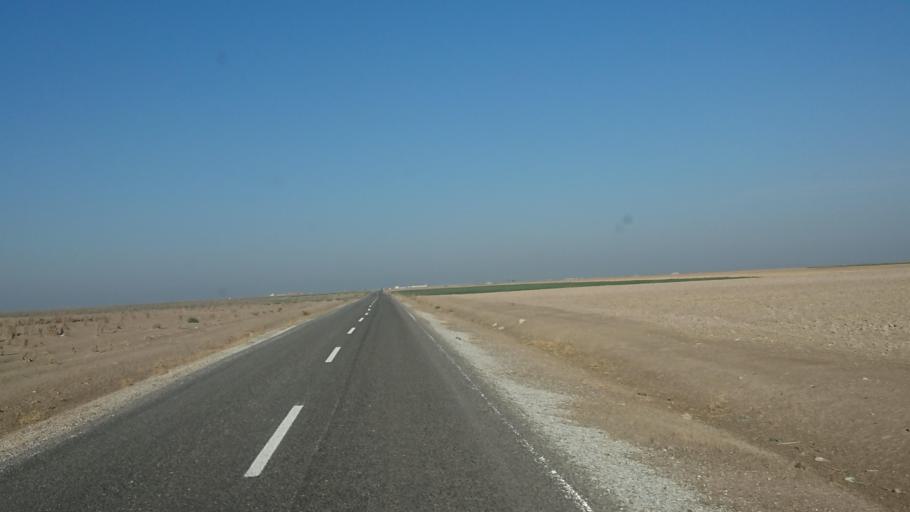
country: TR
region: Aksaray
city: Yesilova
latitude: 38.3878
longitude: 33.7699
